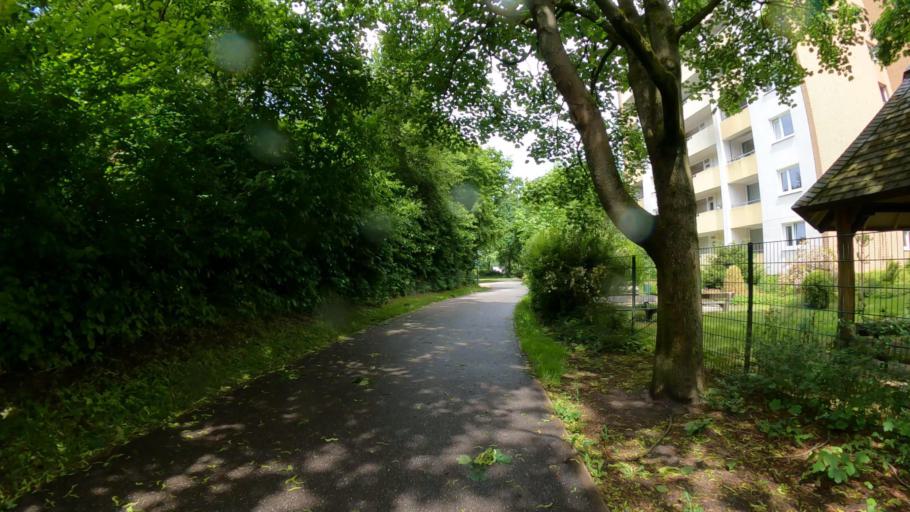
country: DE
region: Schleswig-Holstein
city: Norderstedt
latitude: 53.6865
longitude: 9.9885
